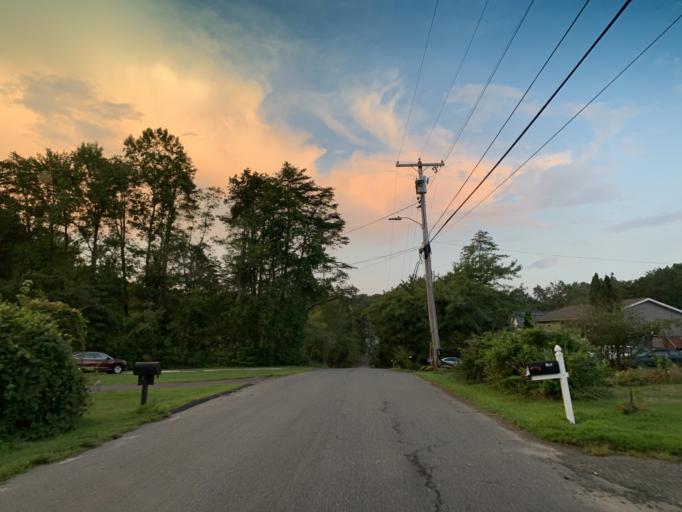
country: US
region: Maryland
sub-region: Harford County
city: Edgewood
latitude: 39.4164
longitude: -76.3371
